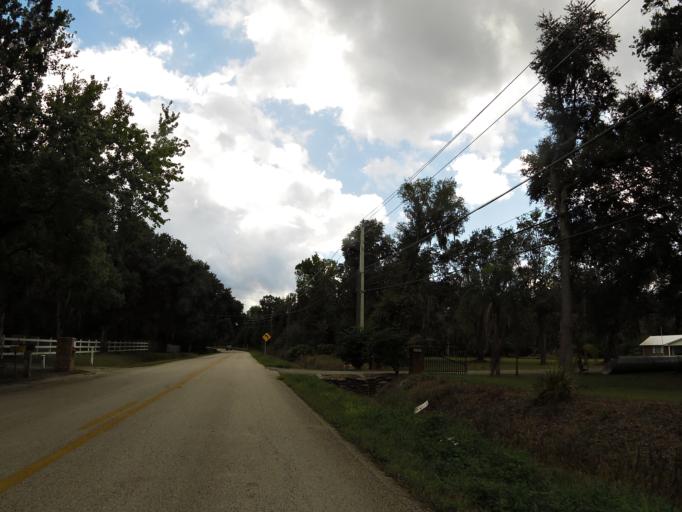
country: US
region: Florida
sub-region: Saint Johns County
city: Saint Augustine South
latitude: 29.8397
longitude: -81.5003
